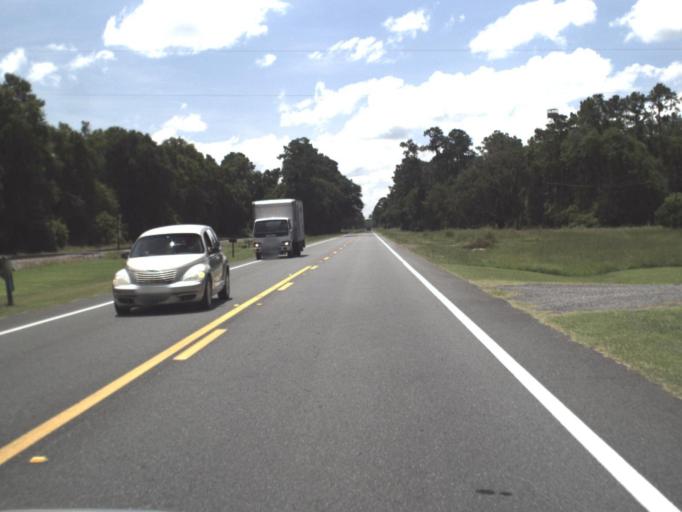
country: US
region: Florida
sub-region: Suwannee County
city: Wellborn
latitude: 30.3561
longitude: -82.7811
